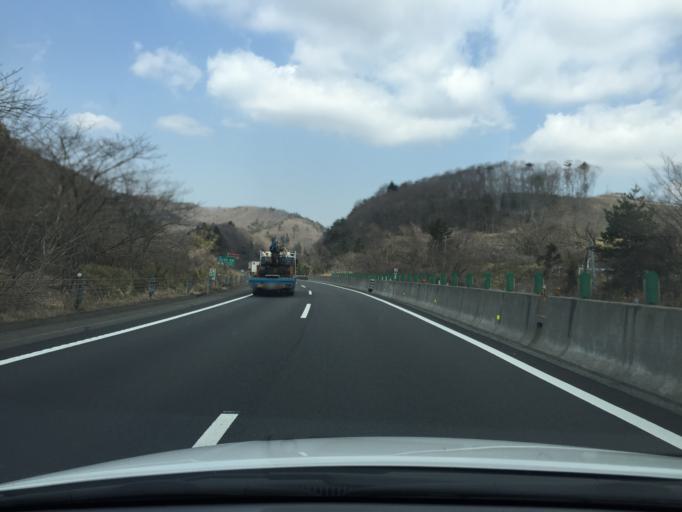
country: JP
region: Miyagi
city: Sendai
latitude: 38.2507
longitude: 140.8165
